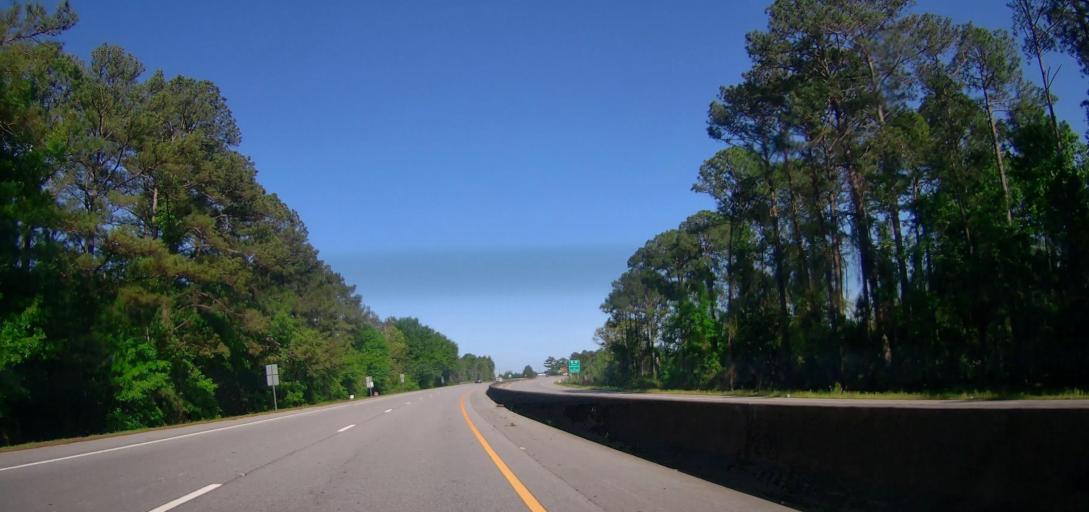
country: US
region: Georgia
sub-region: Houston County
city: Robins Air Force Base
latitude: 32.5944
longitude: -83.5981
